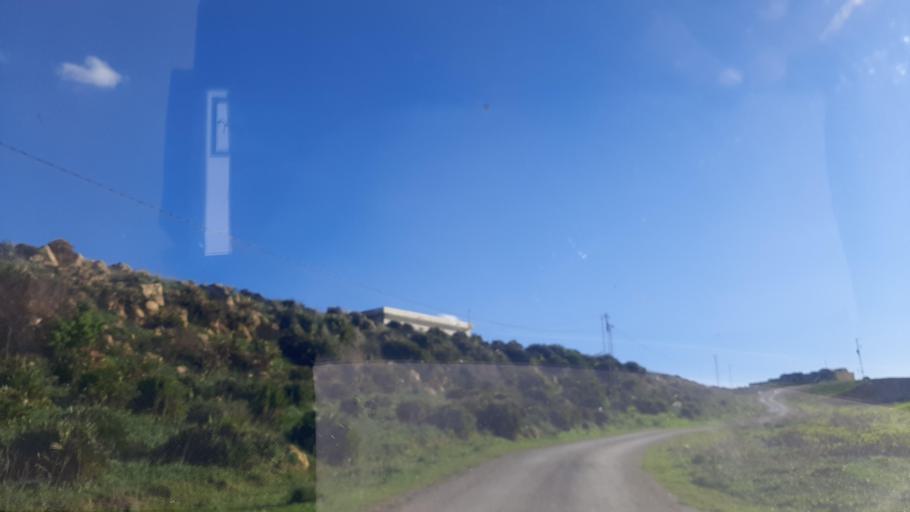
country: TN
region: Nabul
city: El Mida
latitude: 36.8097
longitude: 10.8458
